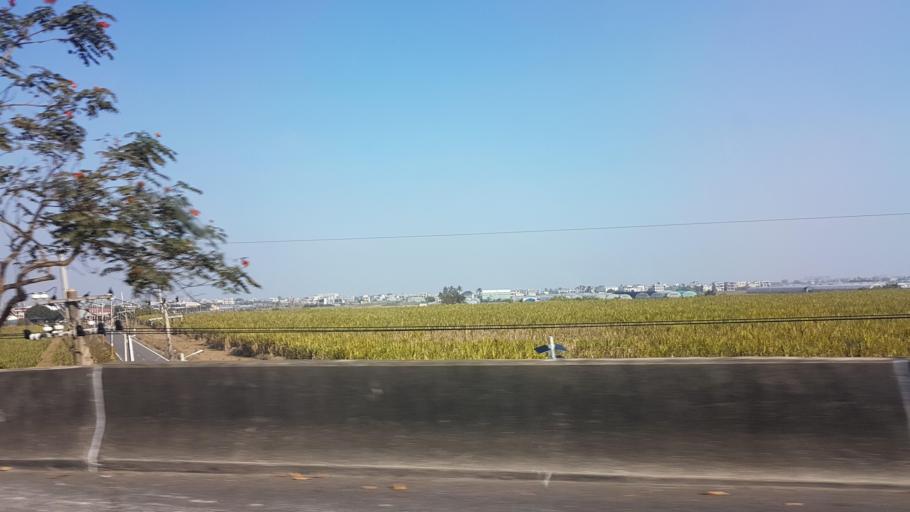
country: TW
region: Taiwan
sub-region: Chiayi
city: Taibao
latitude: 23.4269
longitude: 120.3460
